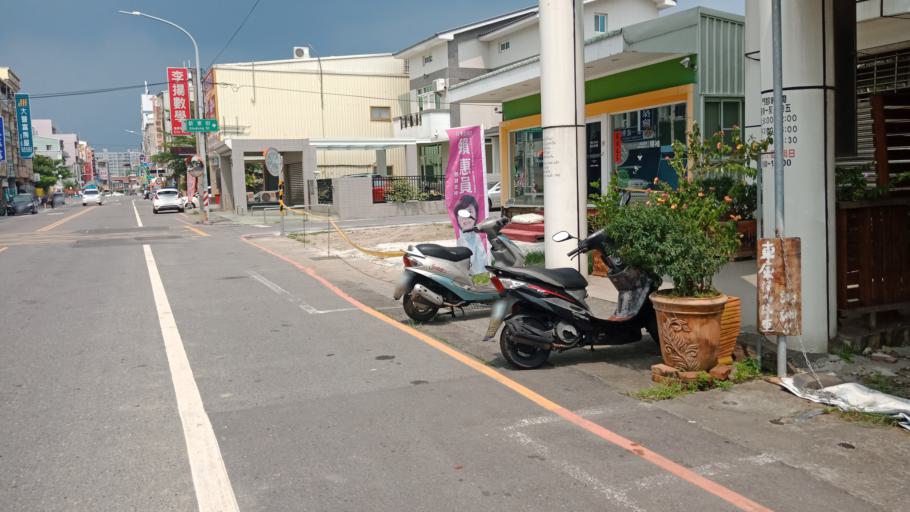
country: TW
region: Taiwan
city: Xinying
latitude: 23.3086
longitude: 120.3226
